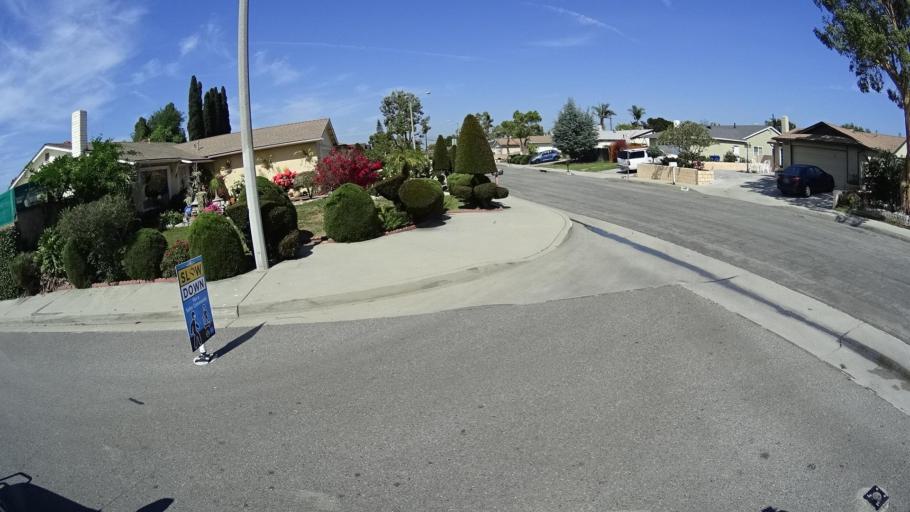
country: US
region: California
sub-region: Los Angeles County
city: South San Jose Hills
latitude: 34.0069
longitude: -117.8893
